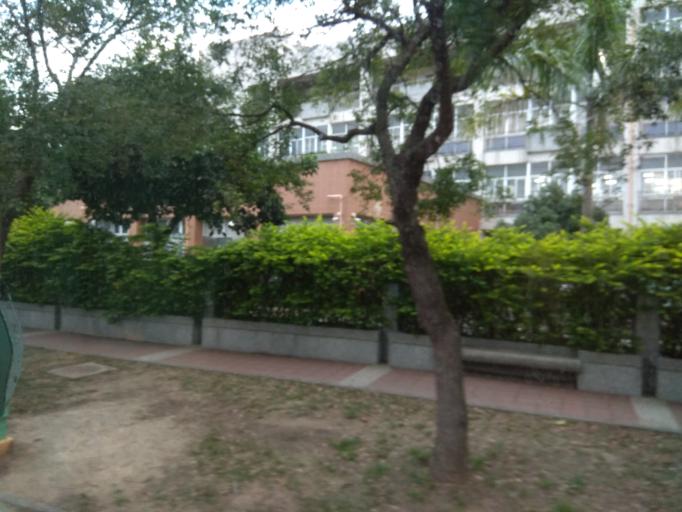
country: TW
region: Taiwan
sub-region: Hsinchu
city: Zhubei
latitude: 24.8195
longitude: 121.0182
